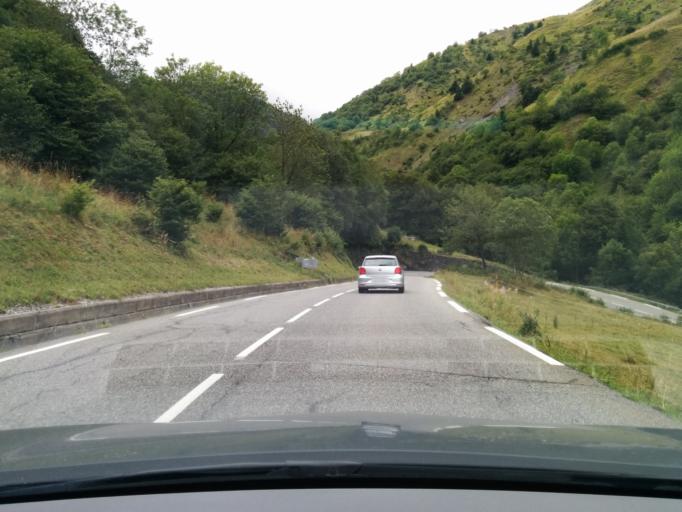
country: FR
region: Midi-Pyrenees
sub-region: Departement des Hautes-Pyrenees
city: Saint-Lary-Soulan
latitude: 42.7821
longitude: 0.2047
